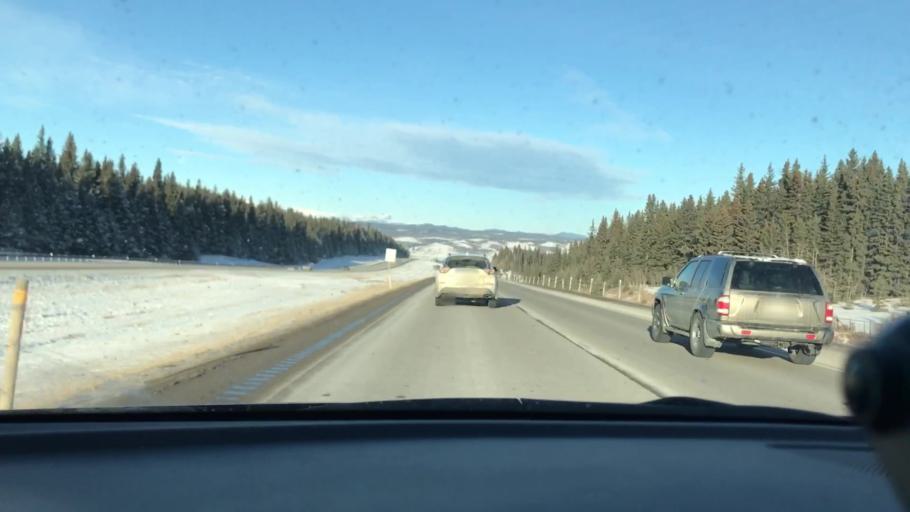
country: CA
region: Alberta
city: Cochrane
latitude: 51.1508
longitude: -114.7401
